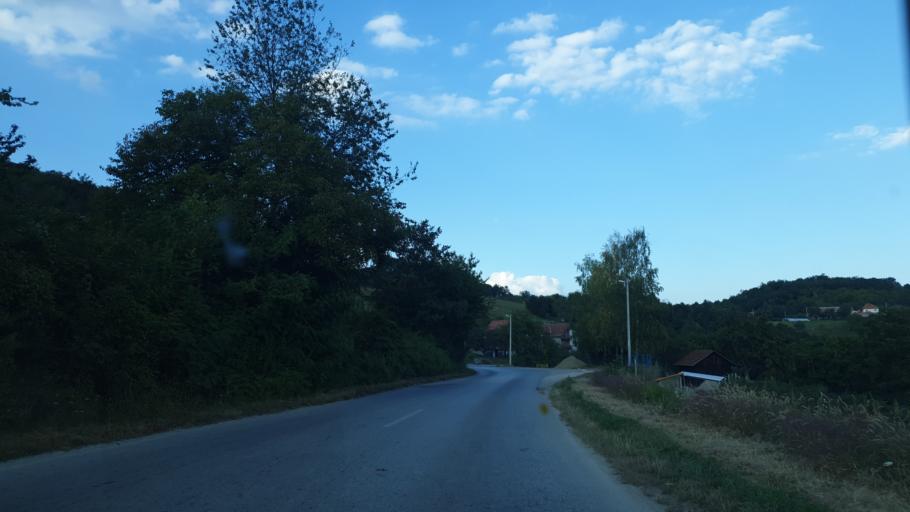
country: RS
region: Central Serbia
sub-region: Zlatiborski Okrug
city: Uzice
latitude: 43.8625
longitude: 19.8862
